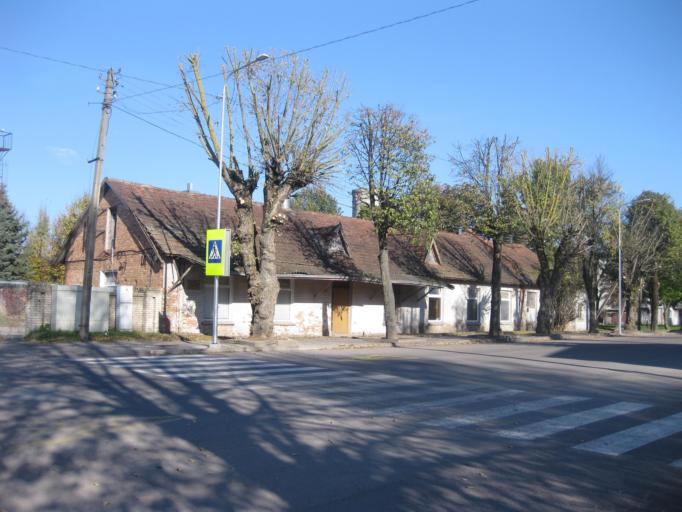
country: LT
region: Kauno apskritis
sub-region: Kauno rajonas
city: Garliava
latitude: 54.8356
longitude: 23.8703
